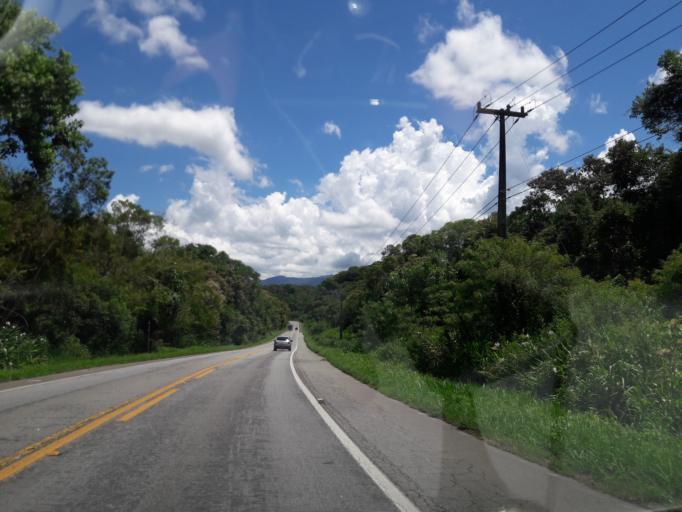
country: BR
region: Parana
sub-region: Antonina
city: Antonina
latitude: -25.4486
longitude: -48.8000
